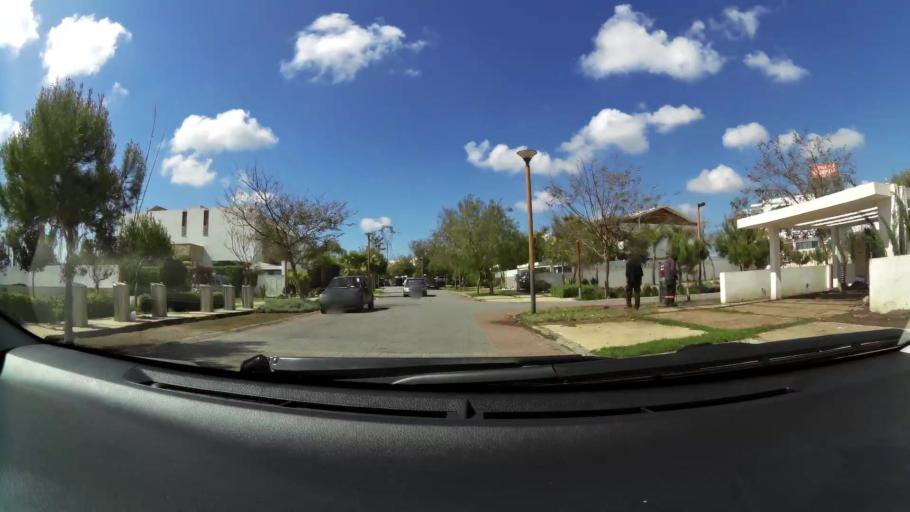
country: MA
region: Grand Casablanca
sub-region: Nouaceur
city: Bouskoura
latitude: 33.4936
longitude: -7.5969
